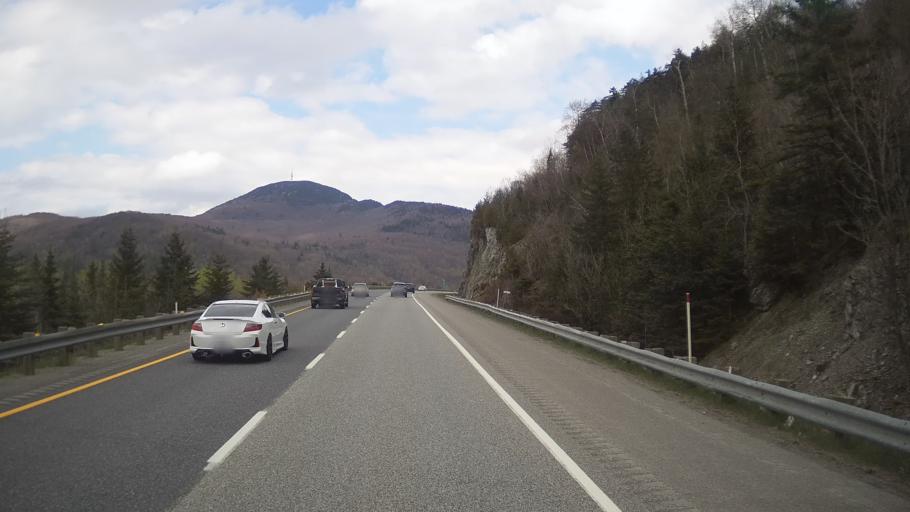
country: CA
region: Quebec
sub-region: Estrie
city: Magog
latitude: 45.2872
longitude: -72.2710
